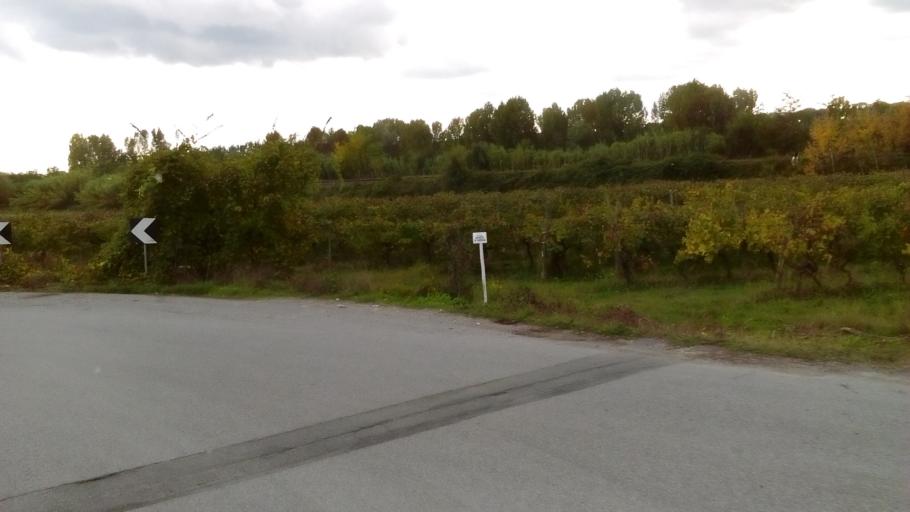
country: IT
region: Tuscany
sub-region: Province of Florence
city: Castelfiorentino
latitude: 43.5924
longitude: 10.9827
